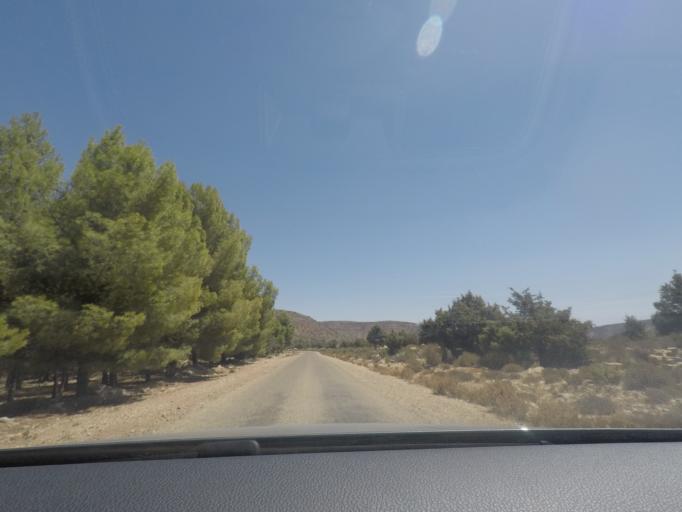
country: MA
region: Souss-Massa-Draa
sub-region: Agadir-Ida-ou-Tnan
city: Tadrart
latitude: 30.7441
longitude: -9.3608
